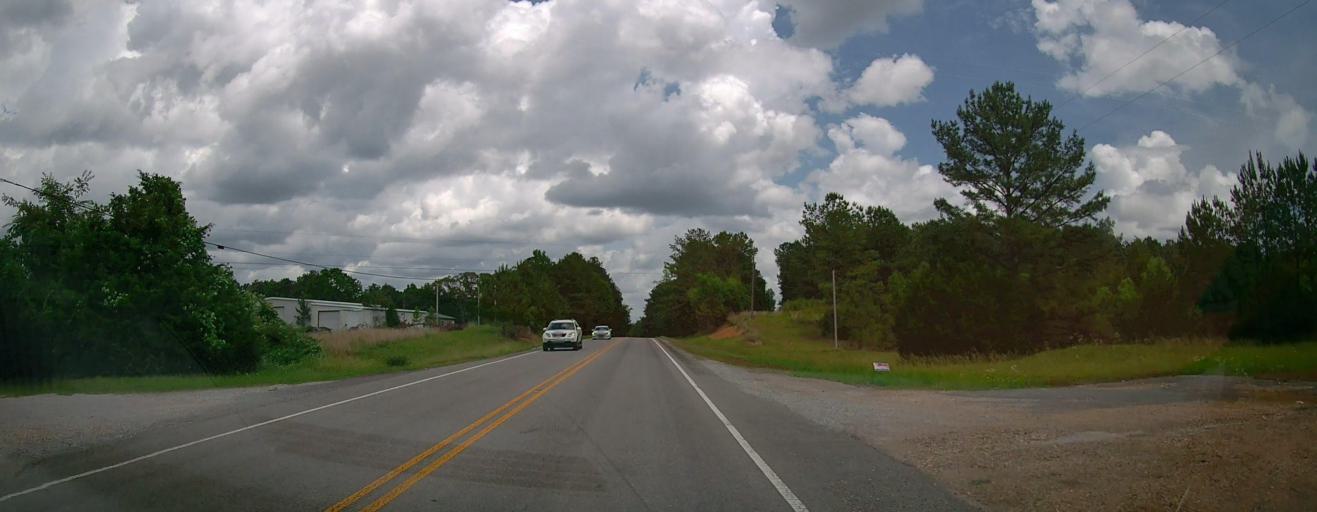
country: US
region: Alabama
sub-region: Marion County
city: Hamilton
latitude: 34.1229
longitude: -88.0397
